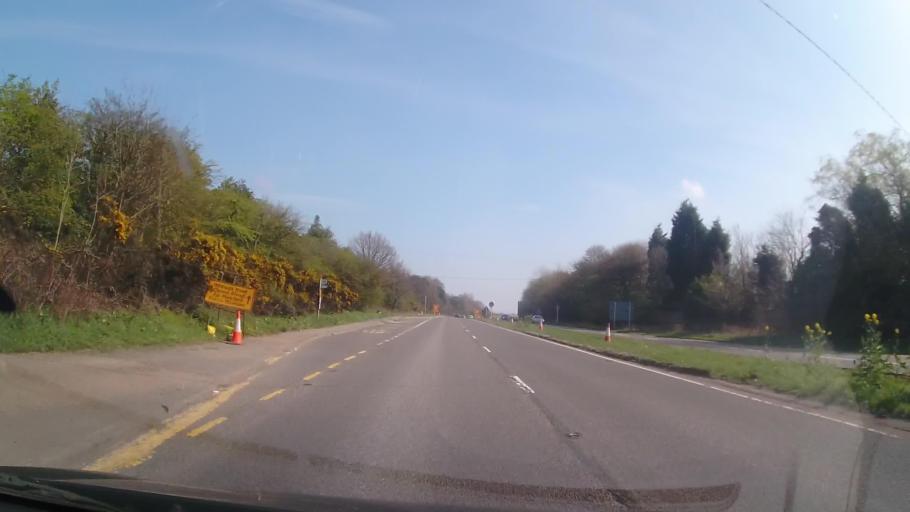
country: GB
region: England
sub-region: Leicestershire
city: Markfield
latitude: 52.6959
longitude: -1.2896
